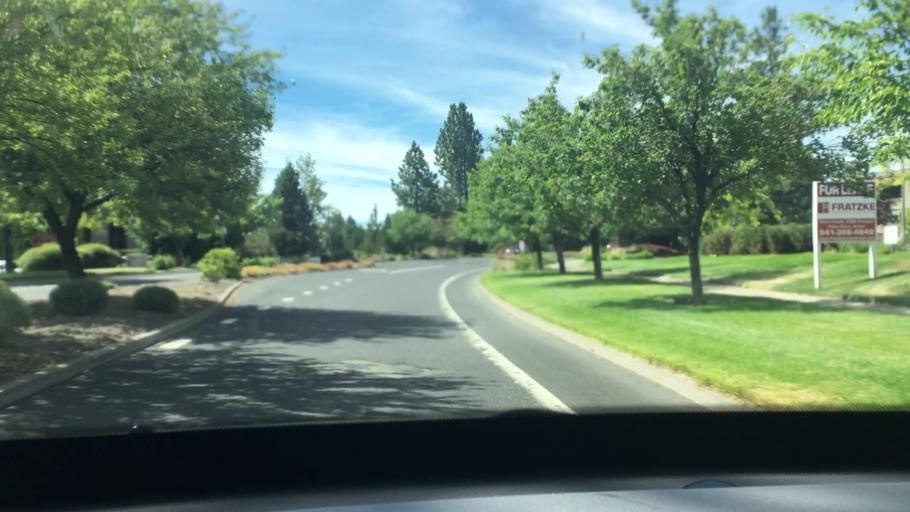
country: US
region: Oregon
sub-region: Deschutes County
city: Bend
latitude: 44.0461
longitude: -121.3227
